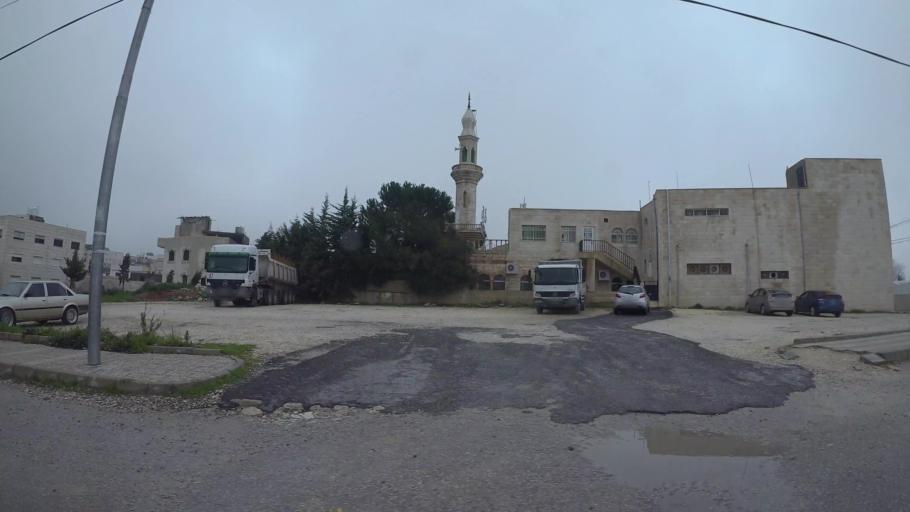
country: JO
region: Amman
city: Al Jubayhah
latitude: 32.0252
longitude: 35.8359
